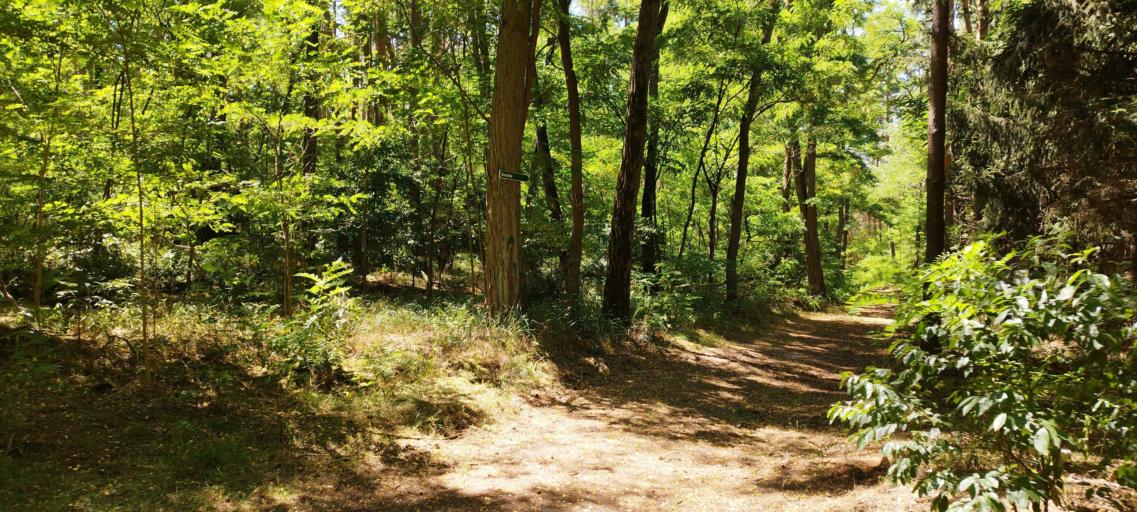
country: DE
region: Brandenburg
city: Reichenwalde
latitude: 52.2757
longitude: 13.9716
